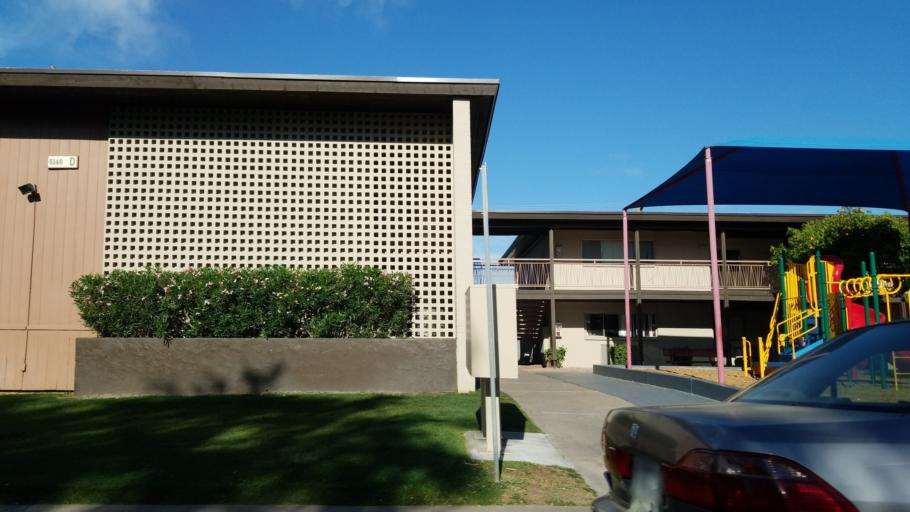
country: US
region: Arizona
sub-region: Maricopa County
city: Phoenix
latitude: 33.5120
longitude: -112.0869
